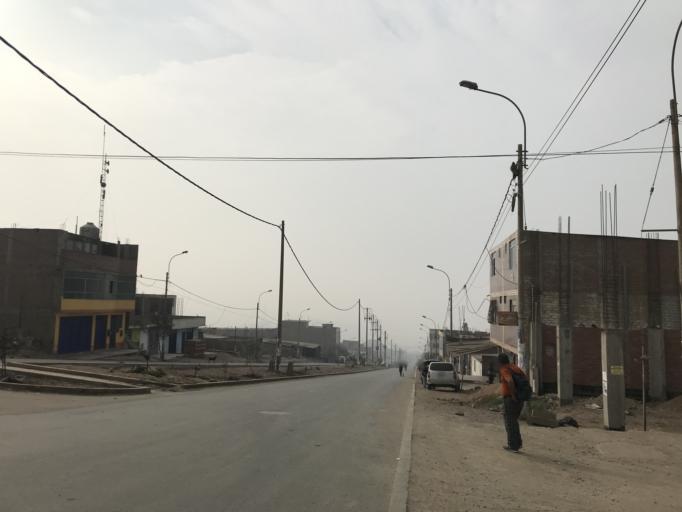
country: PE
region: Lima
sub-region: Lima
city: Carabayllo
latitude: -11.8179
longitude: -77.0463
